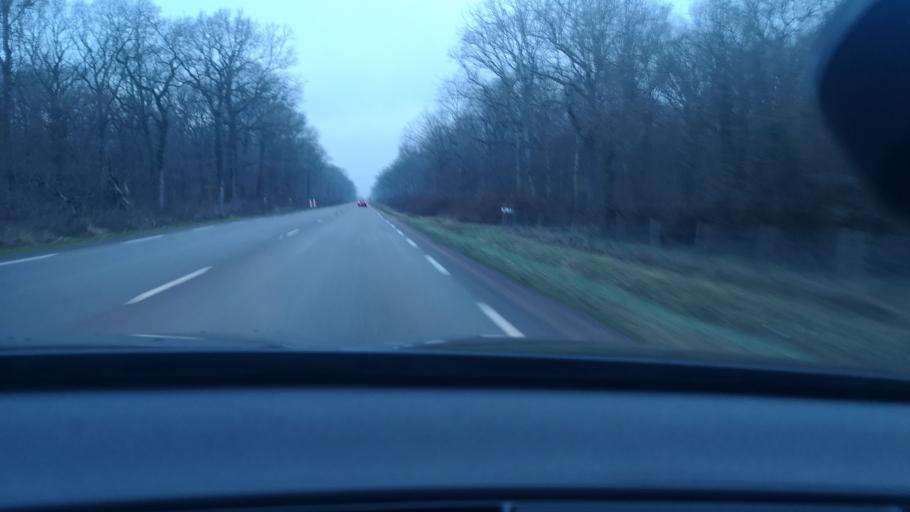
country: FR
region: Bourgogne
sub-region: Departement de Saone-et-Loire
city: Verdun-sur-le-Doubs
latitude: 47.0052
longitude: 5.0412
